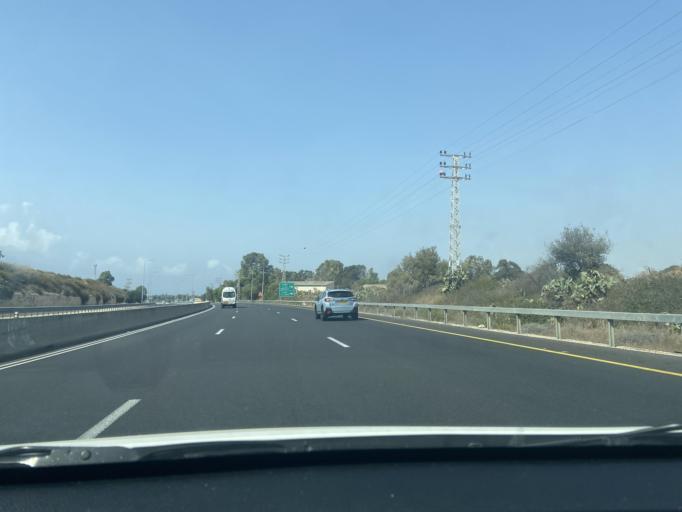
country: IL
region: Northern District
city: `Akko
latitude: 32.9451
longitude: 35.0952
